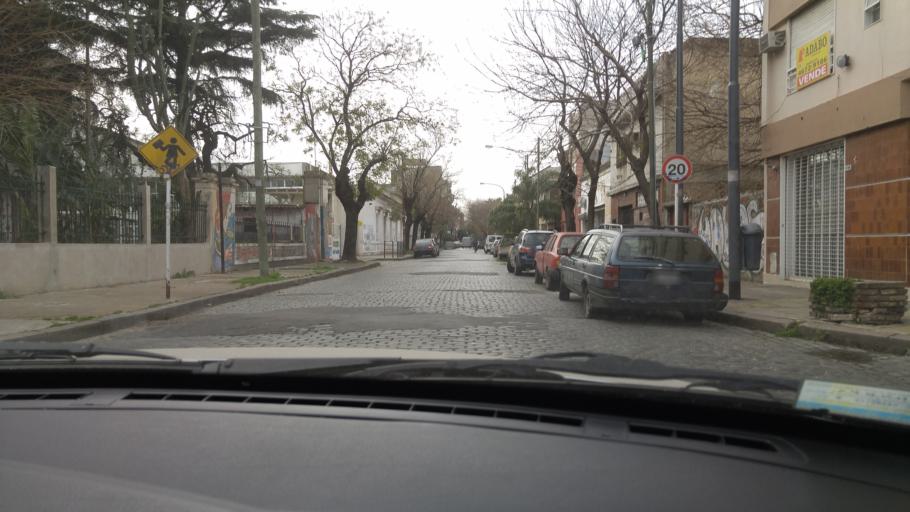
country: AR
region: Buenos Aires F.D.
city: Villa Santa Rita
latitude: -34.6282
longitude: -58.4885
